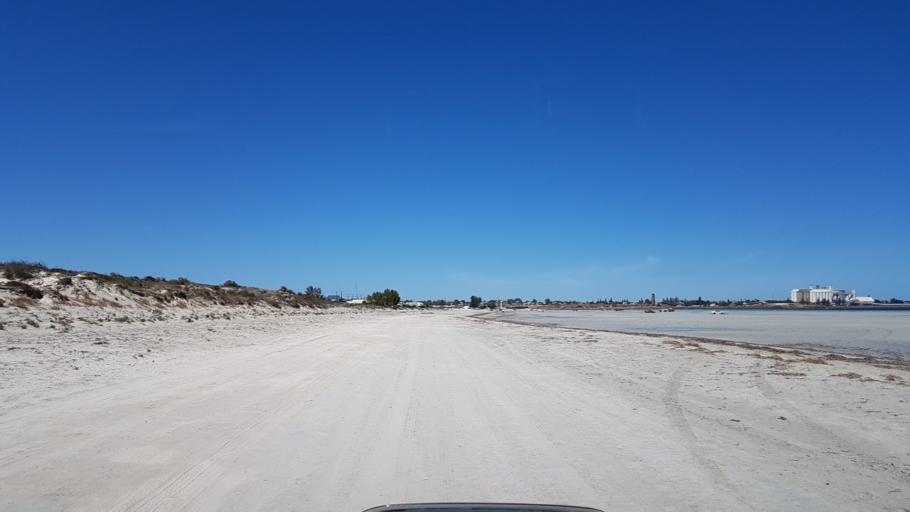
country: AU
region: South Australia
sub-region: Copper Coast
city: Wallaroo
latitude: -33.9086
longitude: 137.6310
